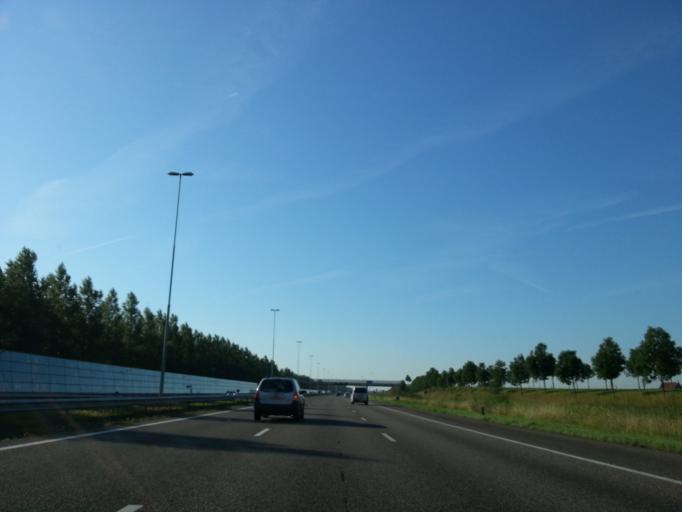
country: NL
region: North Brabant
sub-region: Gemeente Made en Drimmelen
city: Made
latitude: 51.6705
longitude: 4.6743
